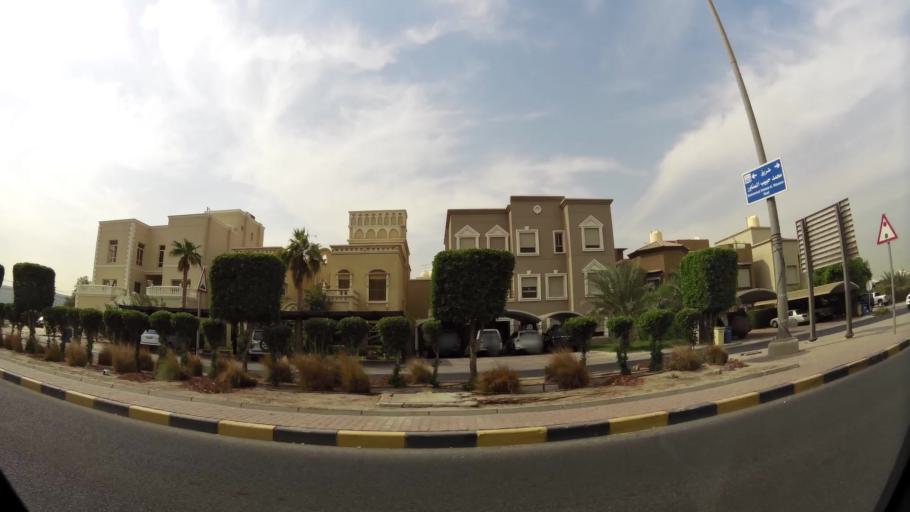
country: KW
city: Bayan
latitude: 29.2868
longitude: 48.0194
